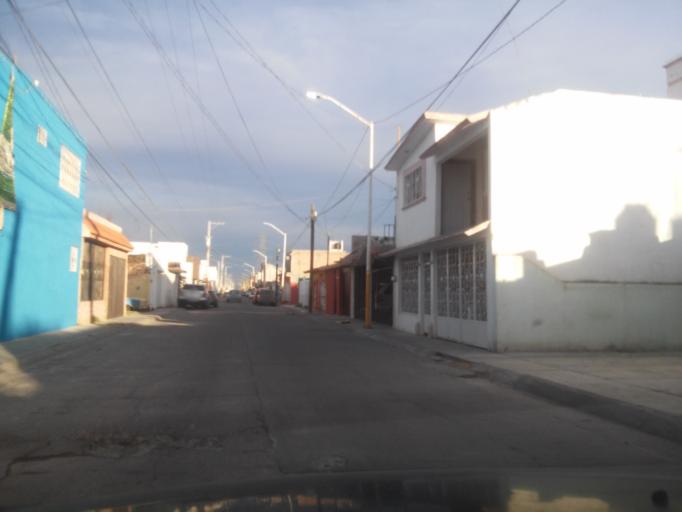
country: MX
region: Durango
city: Victoria de Durango
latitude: 24.0033
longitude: -104.6345
